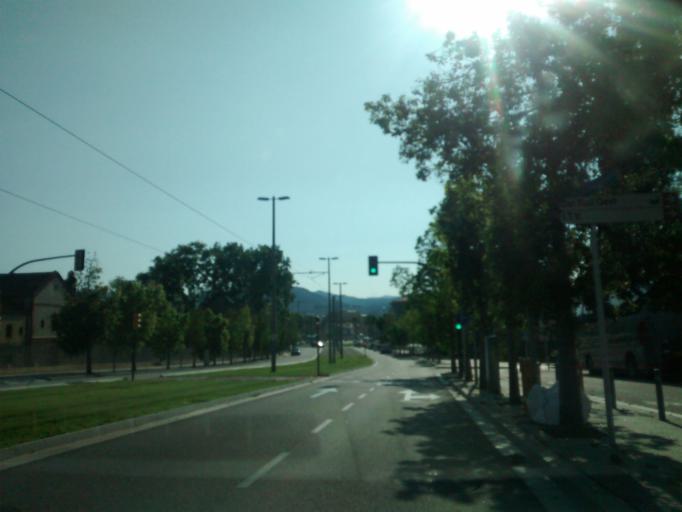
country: ES
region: Catalonia
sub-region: Provincia de Barcelona
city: Sant Feliu de Llobregat
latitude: 41.3798
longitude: 2.0568
